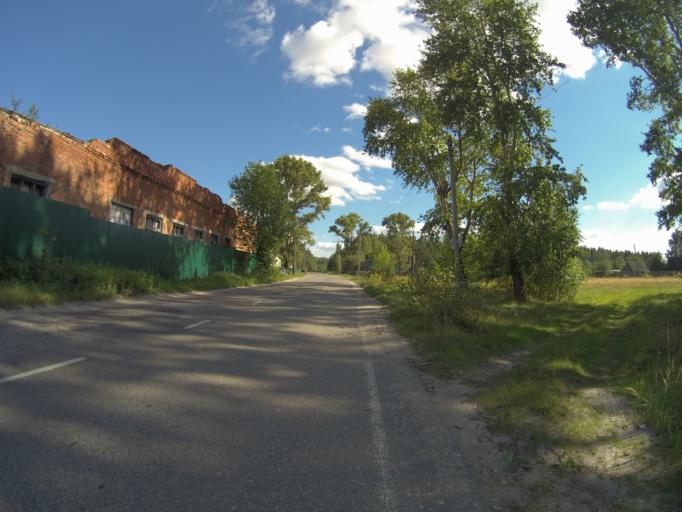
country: RU
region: Vladimir
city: Urshel'skiy
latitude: 55.6702
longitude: 40.2230
